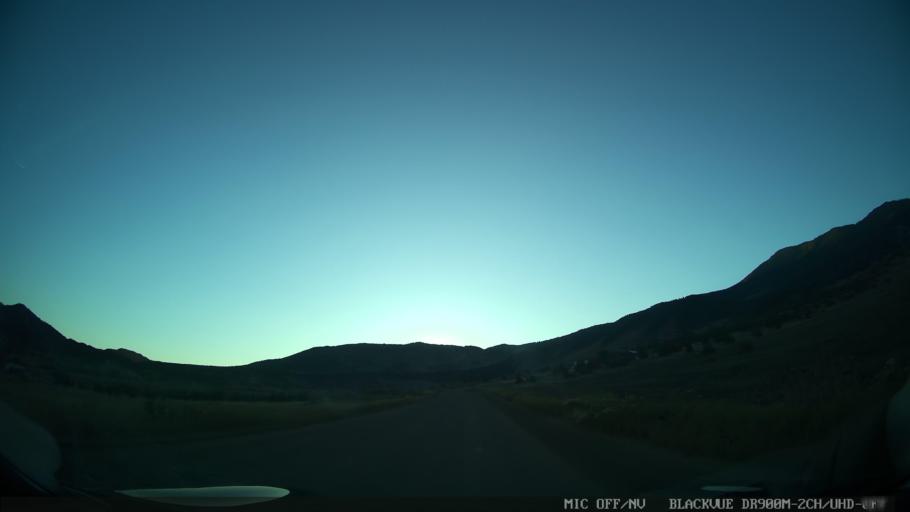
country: US
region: Colorado
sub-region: Eagle County
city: Edwards
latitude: 39.8993
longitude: -106.5986
